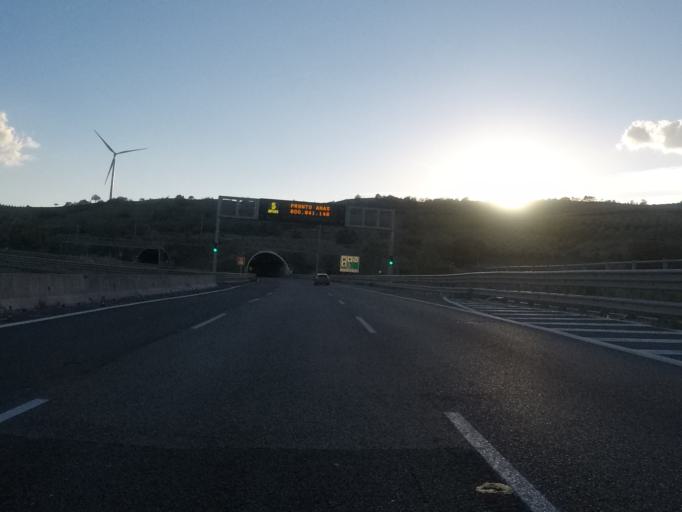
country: IT
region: Campania
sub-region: Provincia di Salerno
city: Serre
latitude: 40.6261
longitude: 15.1828
